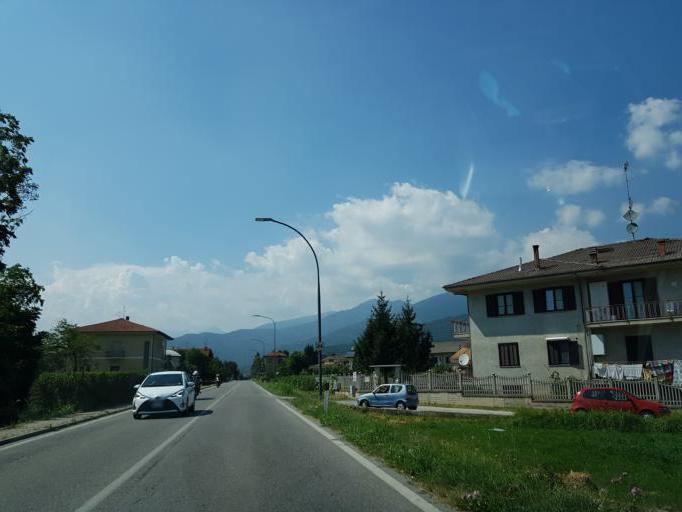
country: IT
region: Piedmont
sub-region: Provincia di Cuneo
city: Dronero
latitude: 44.4583
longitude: 7.3775
